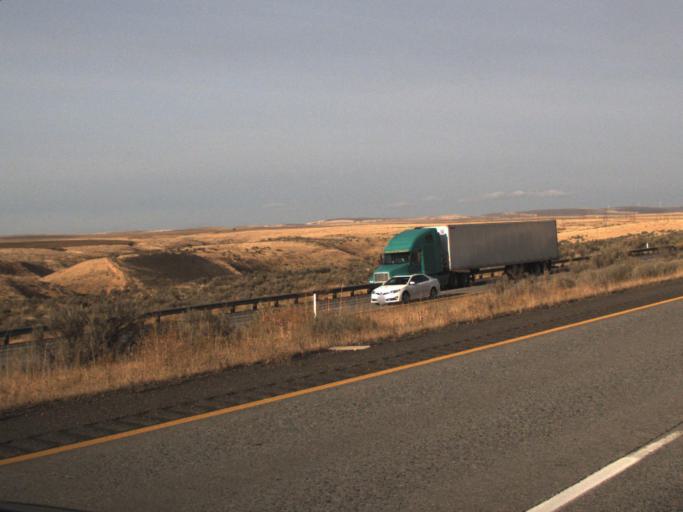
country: US
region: Oregon
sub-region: Umatilla County
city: Umatilla
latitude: 45.9935
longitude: -119.2836
